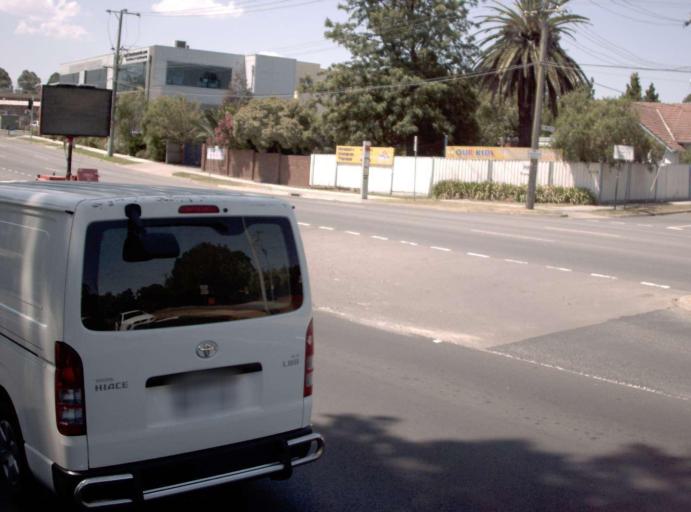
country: AU
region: Victoria
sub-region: Whitehorse
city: Nunawading
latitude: -37.8226
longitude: 145.1750
